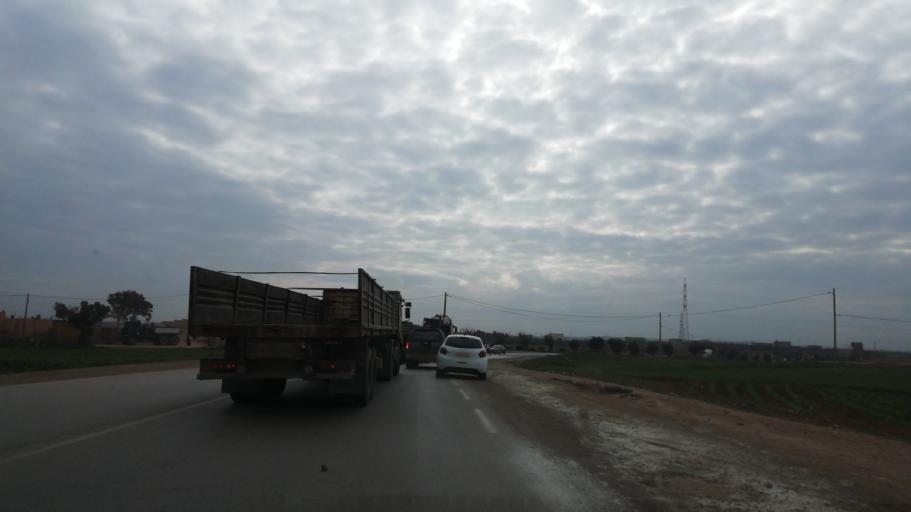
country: DZ
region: Oran
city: Ain el Bya
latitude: 35.7942
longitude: -0.3423
